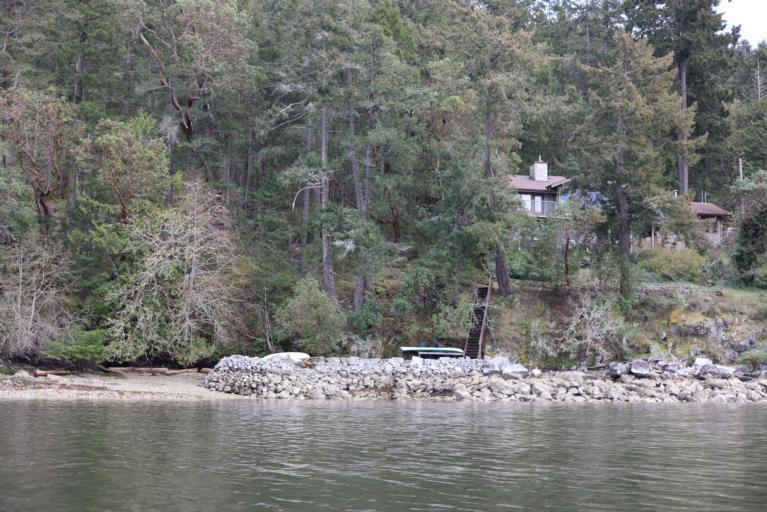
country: CA
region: British Columbia
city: North Saanich
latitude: 48.6185
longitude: -123.4727
